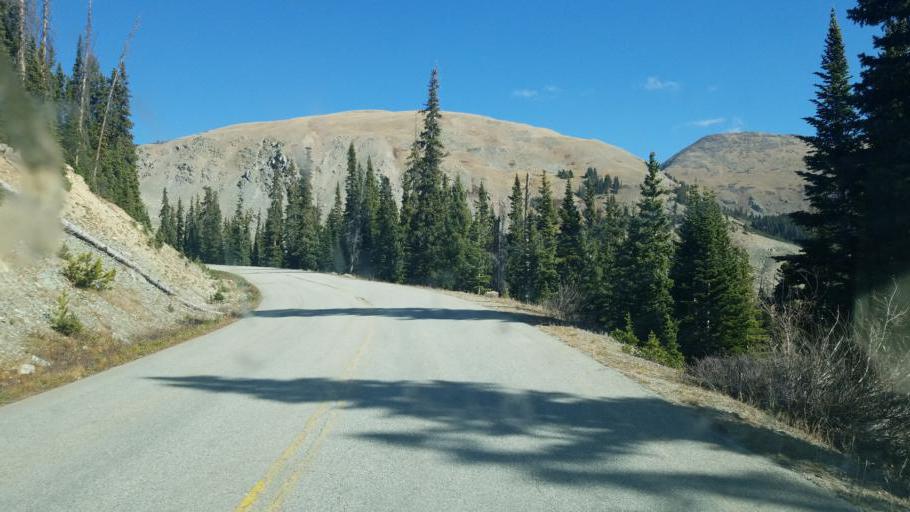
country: US
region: Colorado
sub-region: Chaffee County
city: Buena Vista
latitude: 38.8130
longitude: -106.4022
